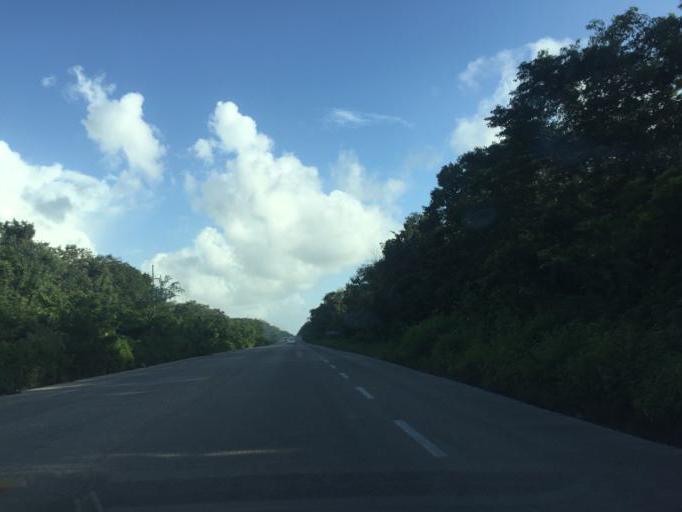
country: MX
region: Quintana Roo
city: Coba
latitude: 20.4857
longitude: -87.6994
